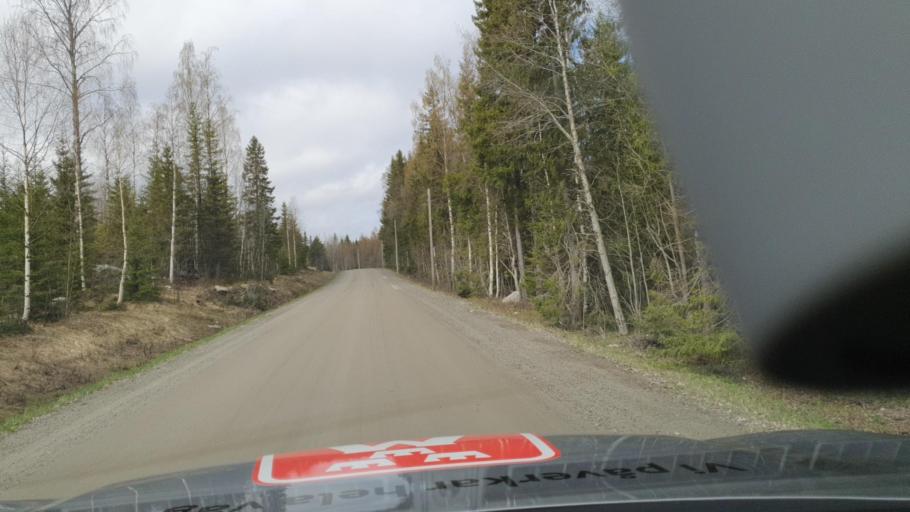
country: SE
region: Vaesterbotten
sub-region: Bjurholms Kommun
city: Bjurholm
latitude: 63.6807
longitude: 18.9851
